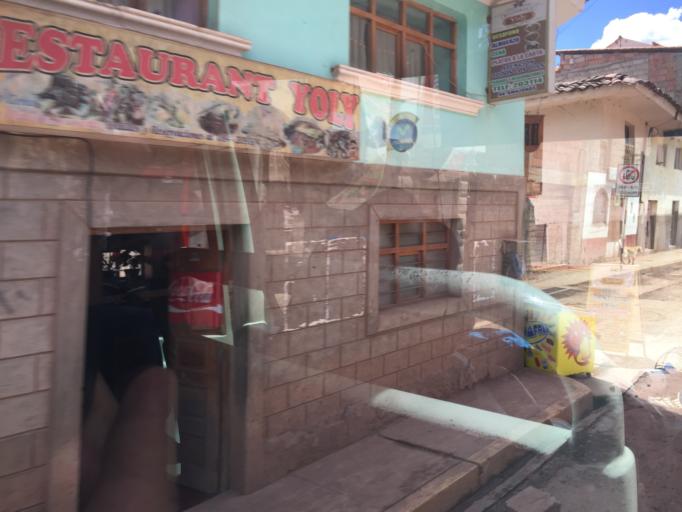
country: PE
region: Cusco
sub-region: Provincia de Calca
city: Pisac
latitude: -13.4233
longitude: -71.8501
